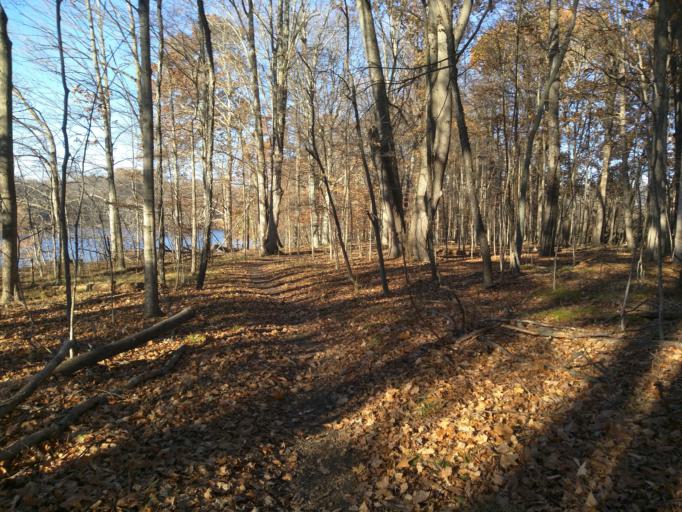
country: US
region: Michigan
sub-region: Eaton County
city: Waverly
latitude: 42.6951
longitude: -84.6140
